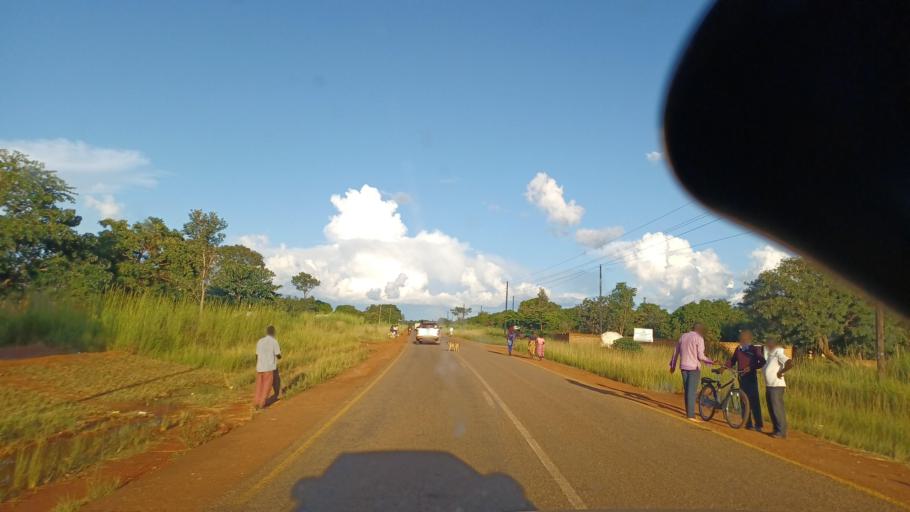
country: ZM
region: North-Western
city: Kalengwa
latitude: -13.1414
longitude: 25.0223
